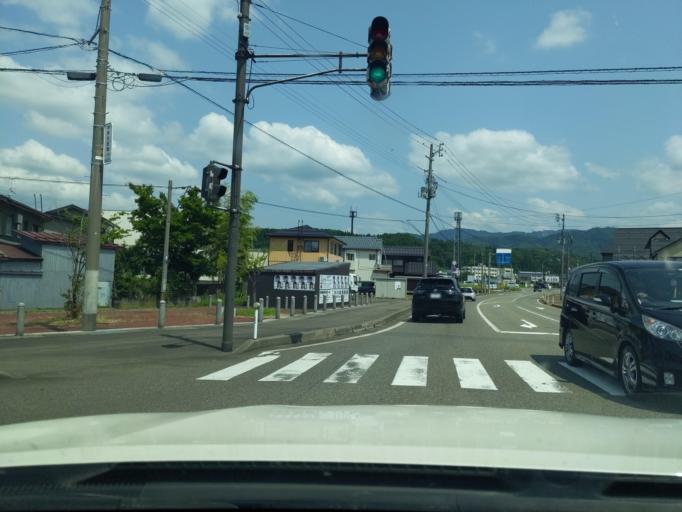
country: JP
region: Niigata
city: Nagaoka
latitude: 37.4265
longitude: 138.8619
